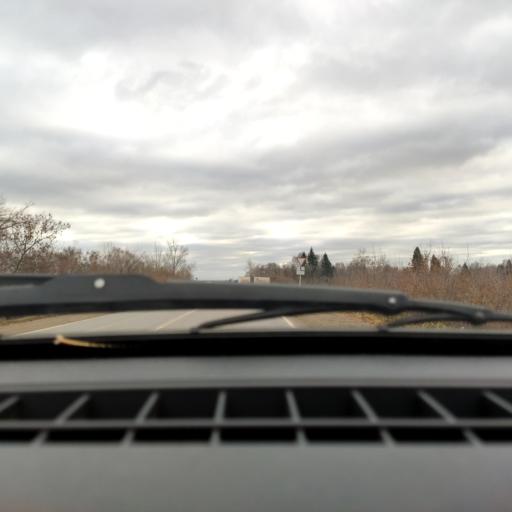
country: RU
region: Bashkortostan
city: Iglino
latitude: 54.7770
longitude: 56.2546
